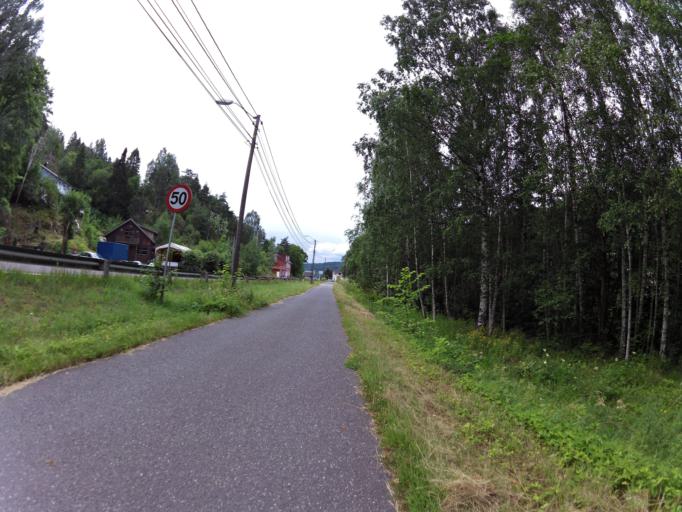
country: NO
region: Akershus
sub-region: As
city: As
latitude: 59.7309
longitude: 10.7367
